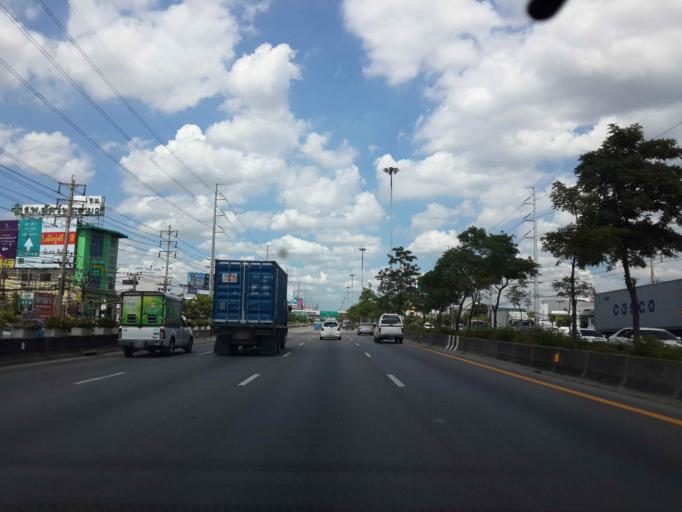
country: TH
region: Bangkok
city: Bang Khun Thian
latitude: 13.6639
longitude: 100.4417
